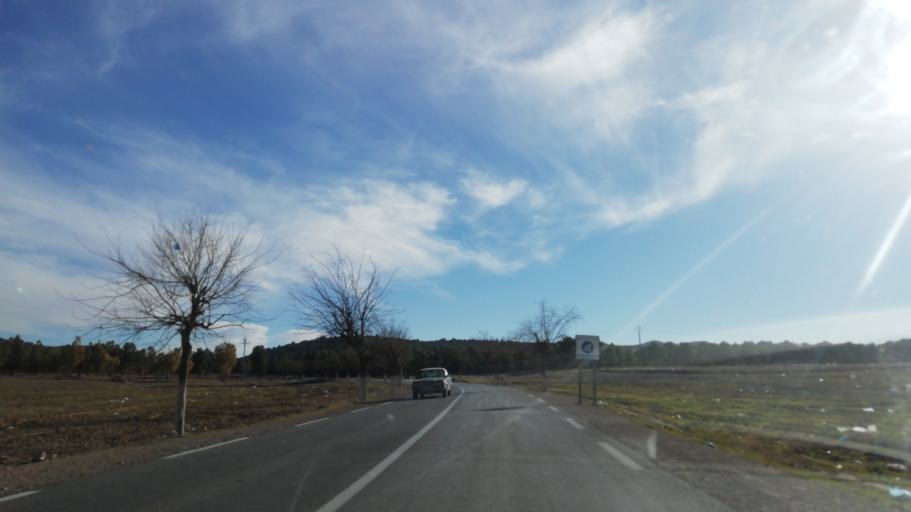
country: DZ
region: Tlemcen
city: Sebdou
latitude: 34.6202
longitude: -1.3349
